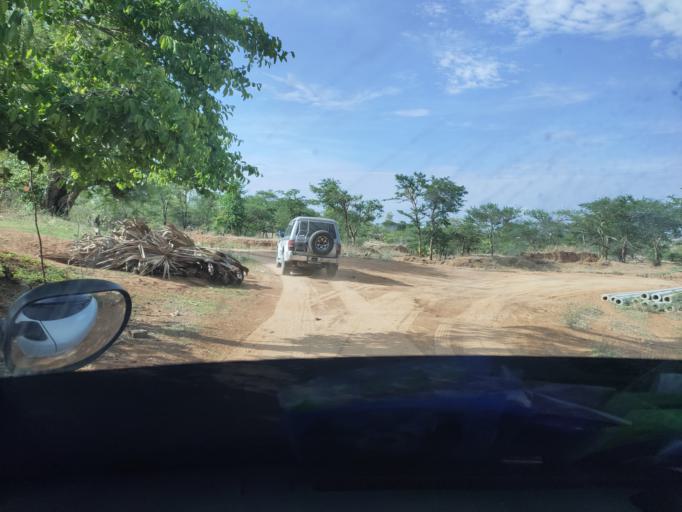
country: MM
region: Magway
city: Chauk
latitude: 20.9562
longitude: 94.9911
